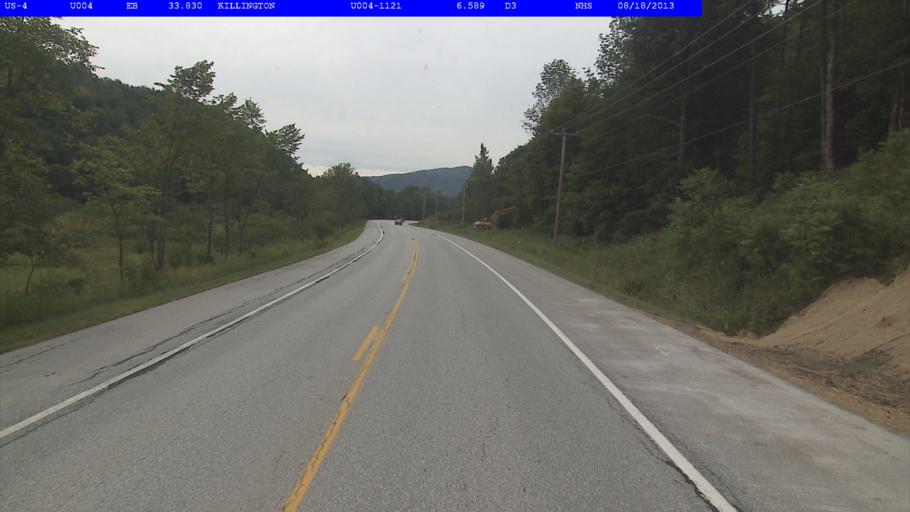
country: US
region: Vermont
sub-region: Rutland County
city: Rutland
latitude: 43.6257
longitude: -72.7619
